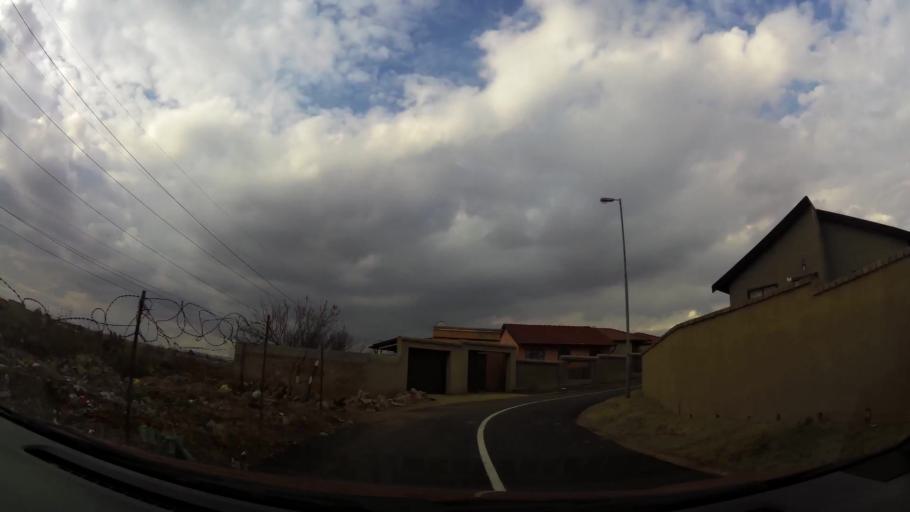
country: ZA
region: Gauteng
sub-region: City of Johannesburg Metropolitan Municipality
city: Soweto
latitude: -26.2418
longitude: 27.8119
